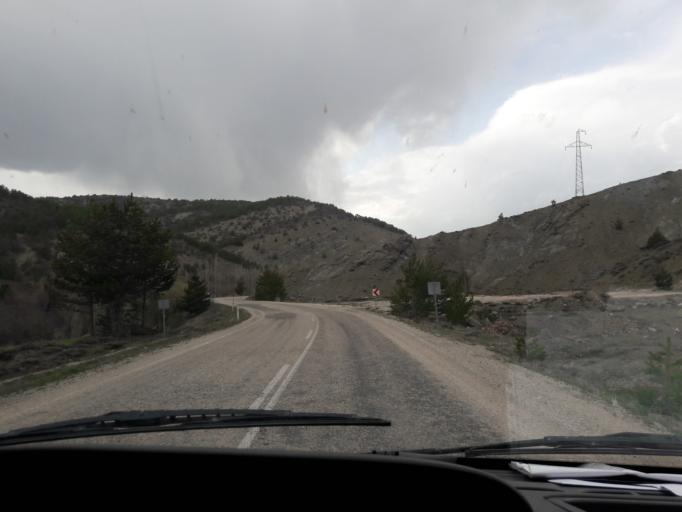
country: TR
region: Giresun
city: Alucra
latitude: 40.2813
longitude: 38.8212
